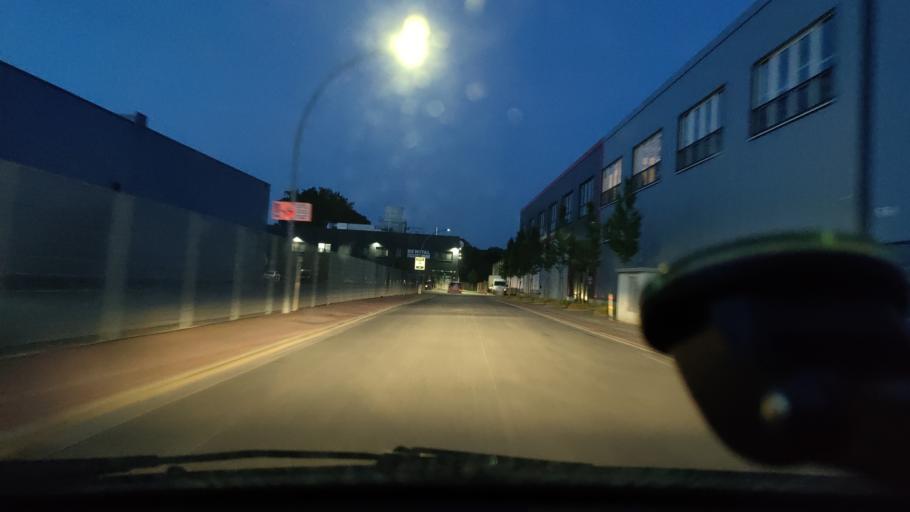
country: DE
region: North Rhine-Westphalia
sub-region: Regierungsbezirk Munster
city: Sudlohn
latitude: 51.9383
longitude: 6.8225
